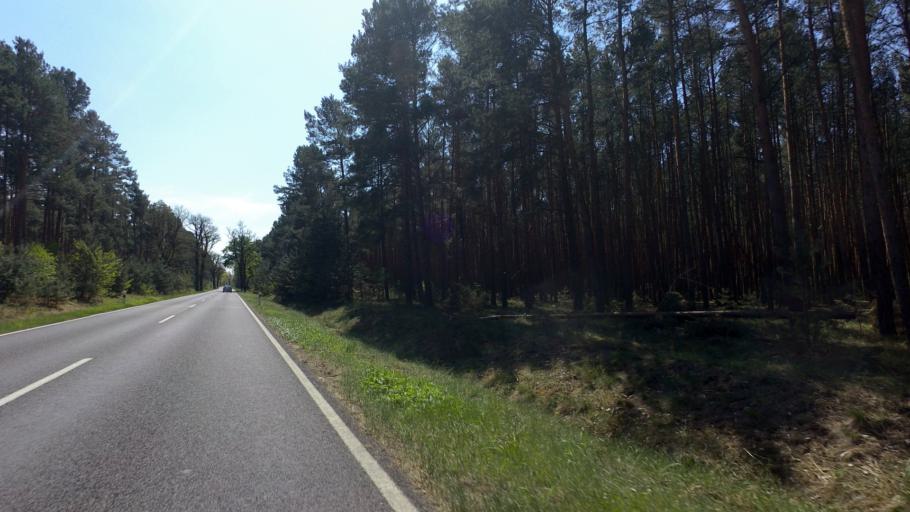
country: DE
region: Brandenburg
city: Halbe
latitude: 52.1327
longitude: 13.7521
